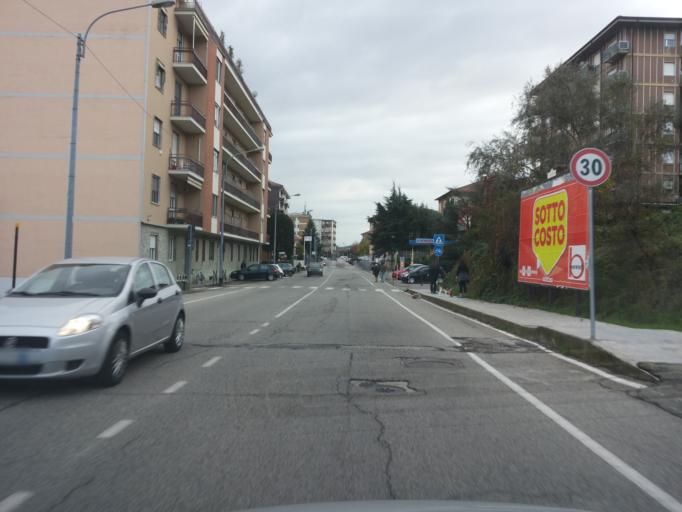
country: IT
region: Piedmont
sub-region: Provincia di Alessandria
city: Casale Monferrato
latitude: 45.1251
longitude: 8.4461
